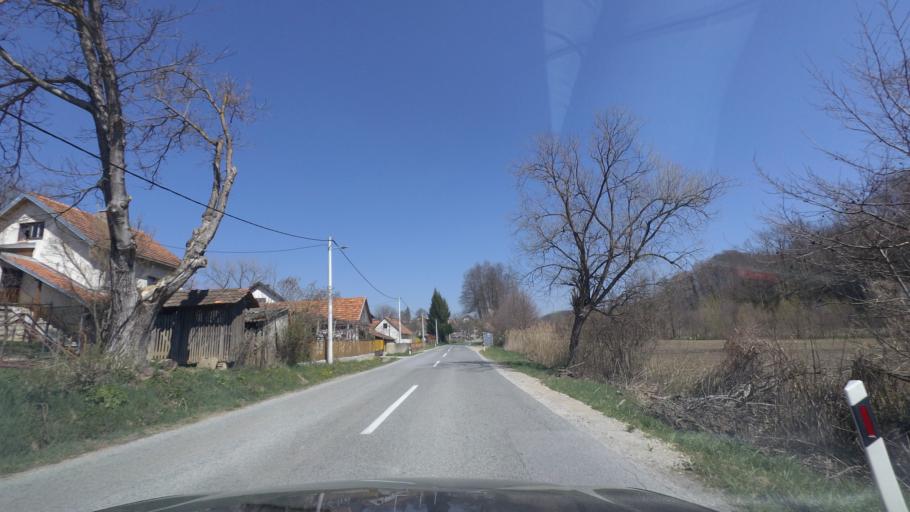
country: HR
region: Karlovacka
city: Vojnic
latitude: 45.3320
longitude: 15.7149
